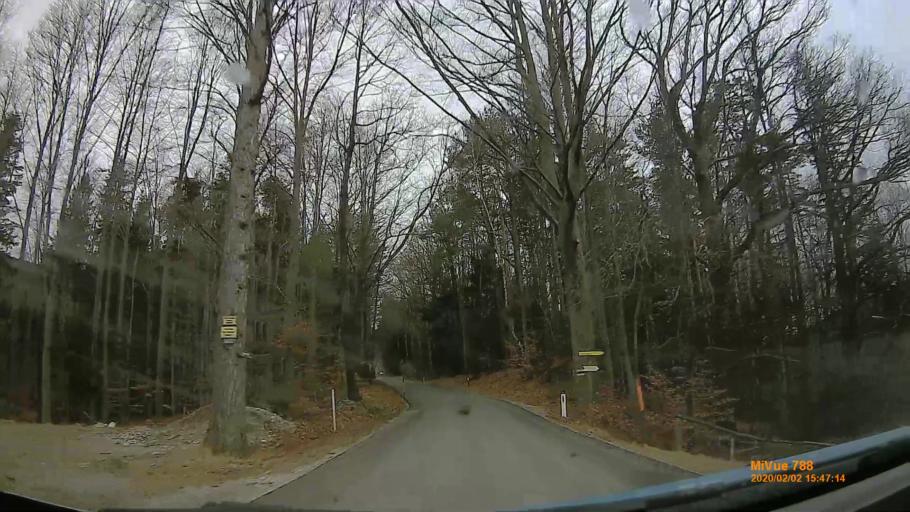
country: AT
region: Lower Austria
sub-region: Politischer Bezirk Neunkirchen
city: Reichenau an der Rax
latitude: 47.6908
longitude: 15.8164
